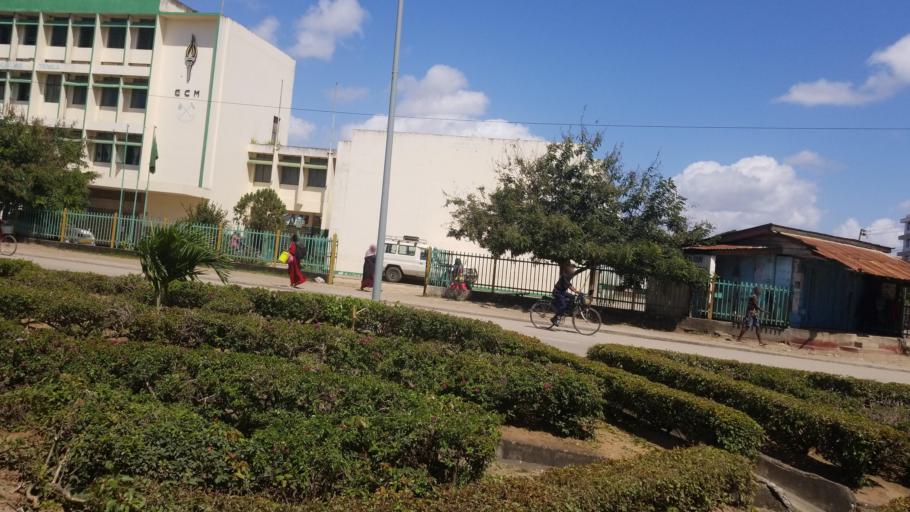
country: TZ
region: Tanga
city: Tanga
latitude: -5.0839
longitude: 39.0976
